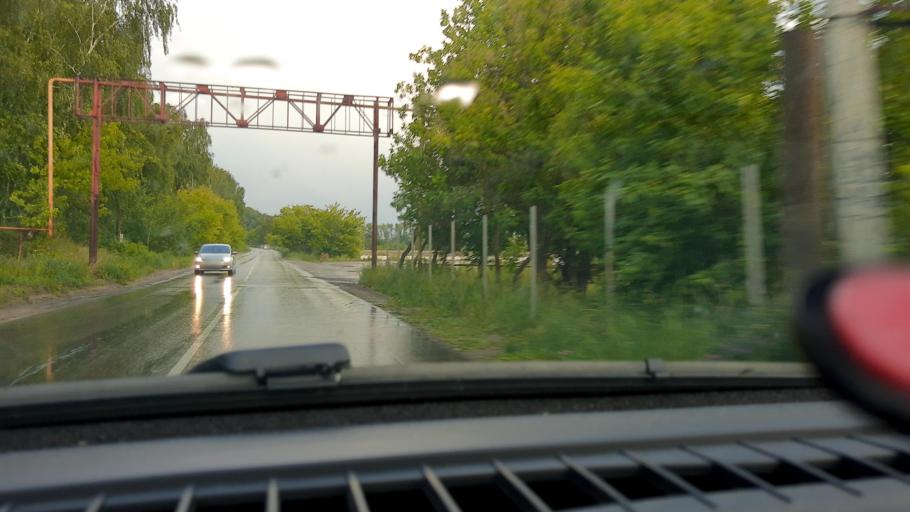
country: RU
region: Nizjnij Novgorod
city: Gorodets
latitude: 56.6717
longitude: 43.4486
